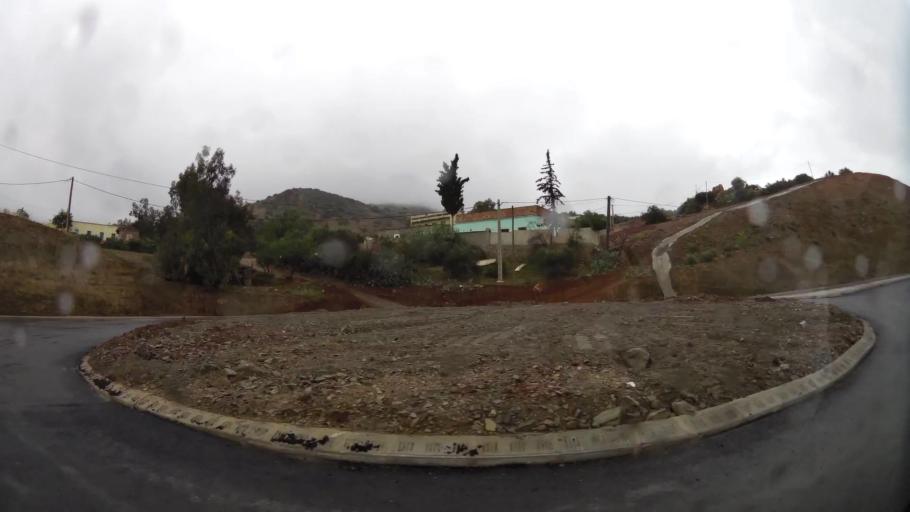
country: MA
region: Taza-Al Hoceima-Taounate
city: Imzourene
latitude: 35.0202
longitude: -3.8207
